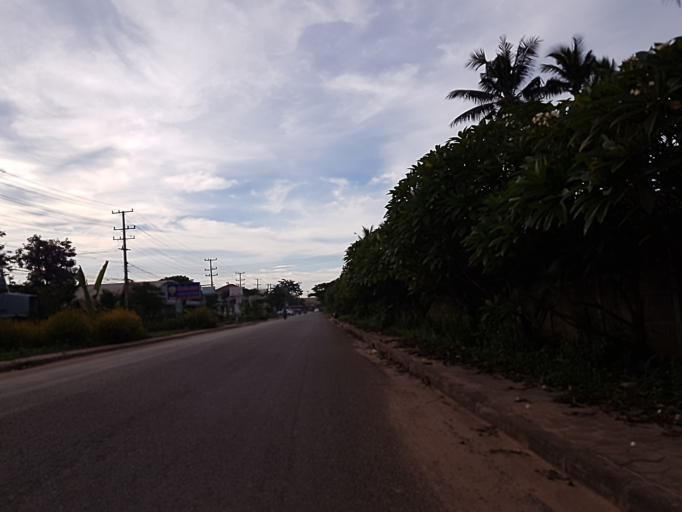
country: TH
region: Nong Khai
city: Si Chiang Mai
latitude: 17.9987
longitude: 102.5628
